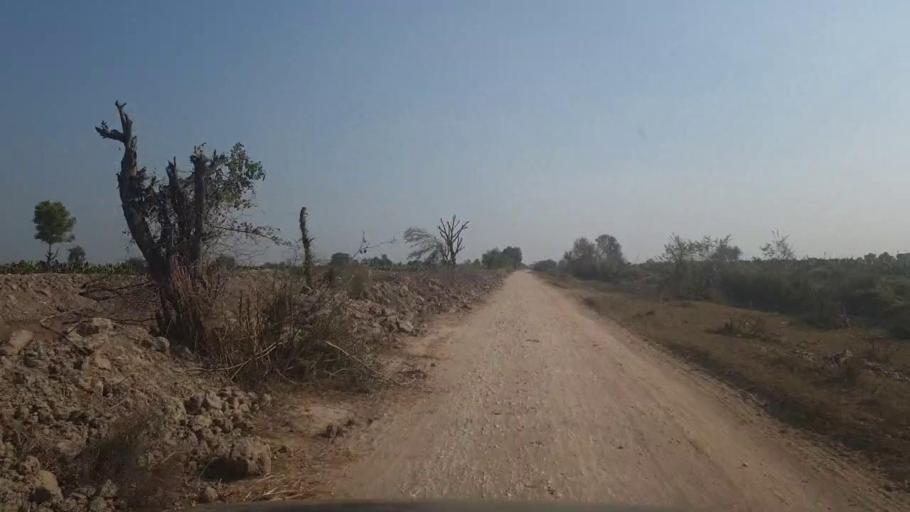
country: PK
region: Sindh
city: Sakrand
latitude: 26.0698
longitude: 68.4296
